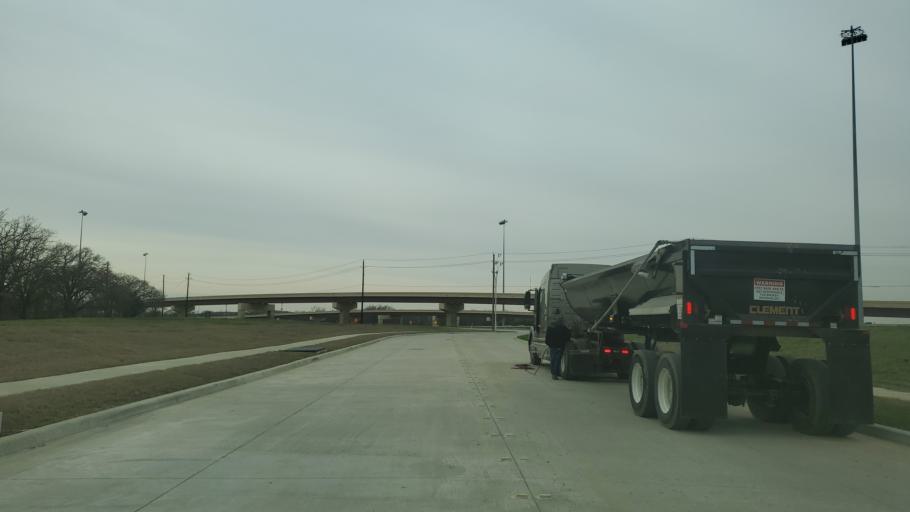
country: US
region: Texas
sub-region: Dallas County
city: Coppell
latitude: 32.9776
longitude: -97.0211
